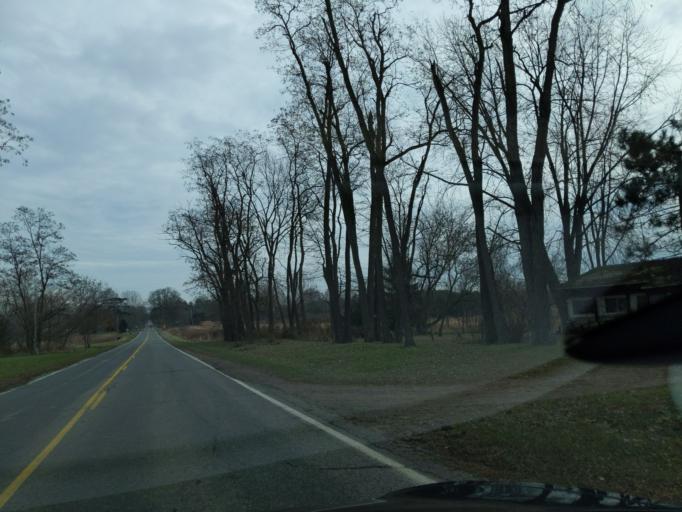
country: US
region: Michigan
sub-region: Ingham County
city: Leslie
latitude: 42.4510
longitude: -84.5019
